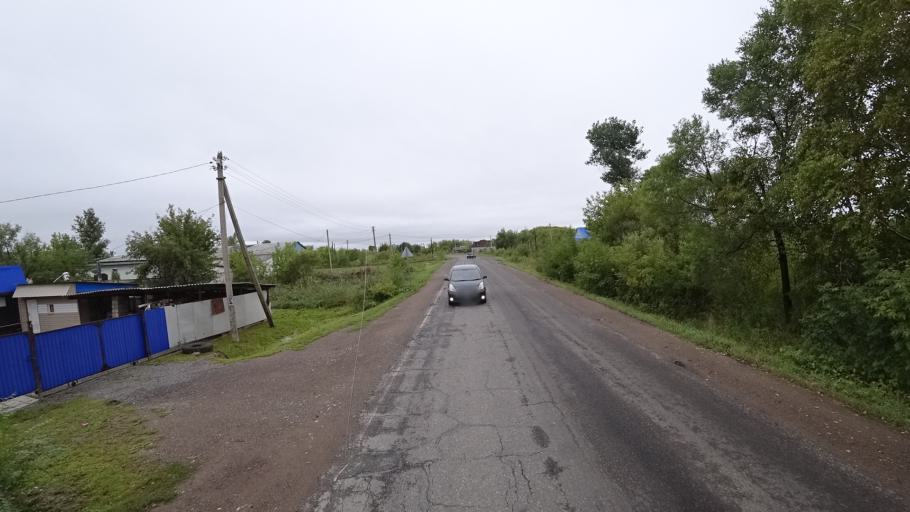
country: RU
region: Primorskiy
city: Monastyrishche
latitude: 44.2045
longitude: 132.4724
